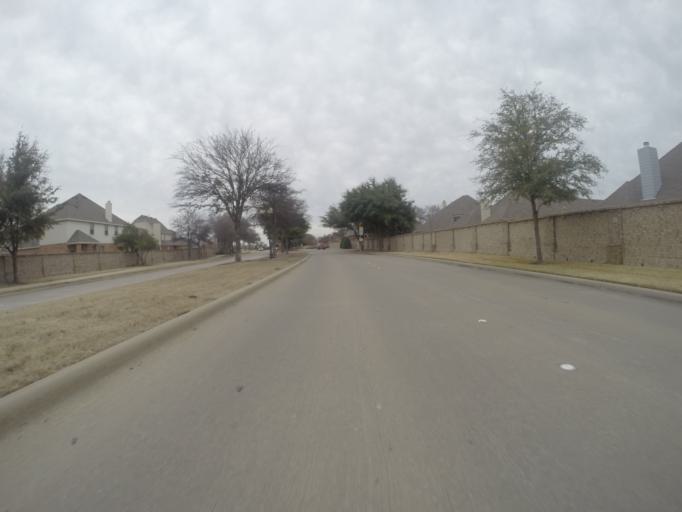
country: US
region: Texas
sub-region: Collin County
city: Saint Paul
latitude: 33.0264
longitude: -96.5687
